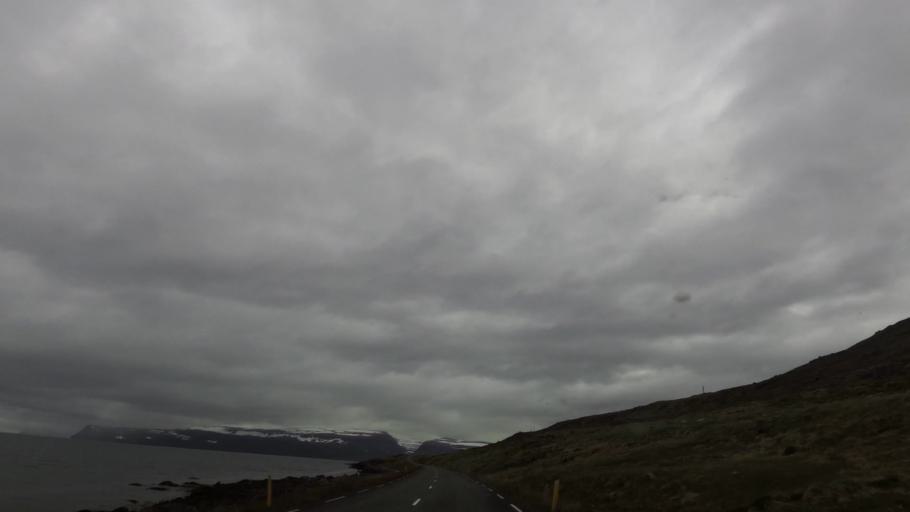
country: IS
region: Westfjords
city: Isafjoerdur
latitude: 66.0397
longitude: -22.7721
